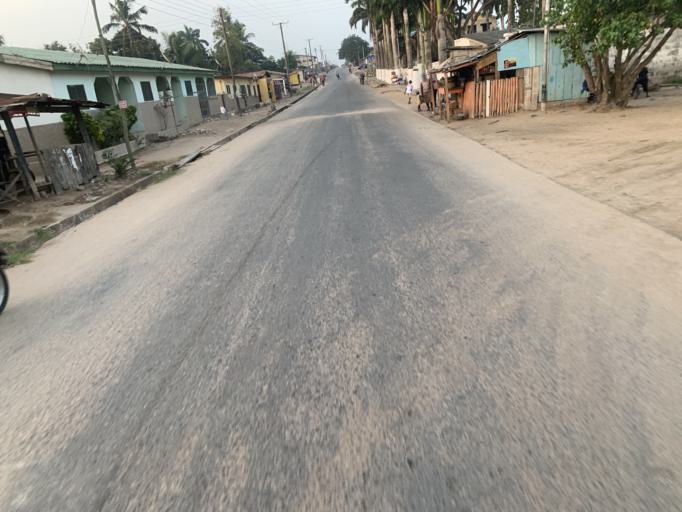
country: GH
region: Central
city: Winneba
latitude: 5.3528
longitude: -0.6266
